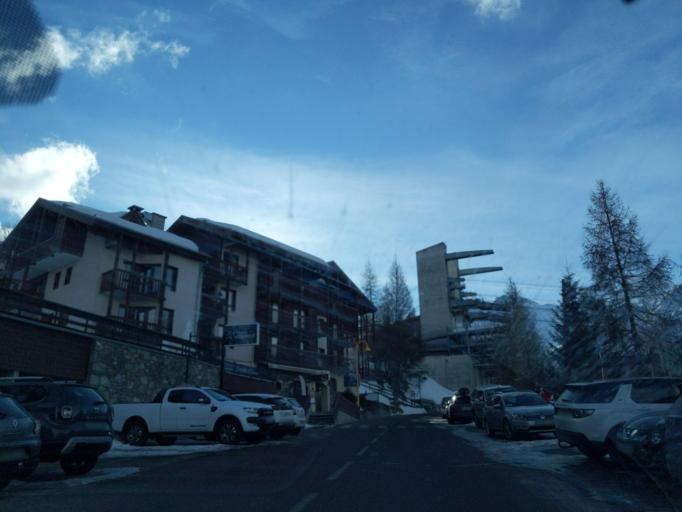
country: FR
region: Rhone-Alpes
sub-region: Departement de la Savoie
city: Bourg-Saint-Maurice
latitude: 45.5522
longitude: 6.7627
